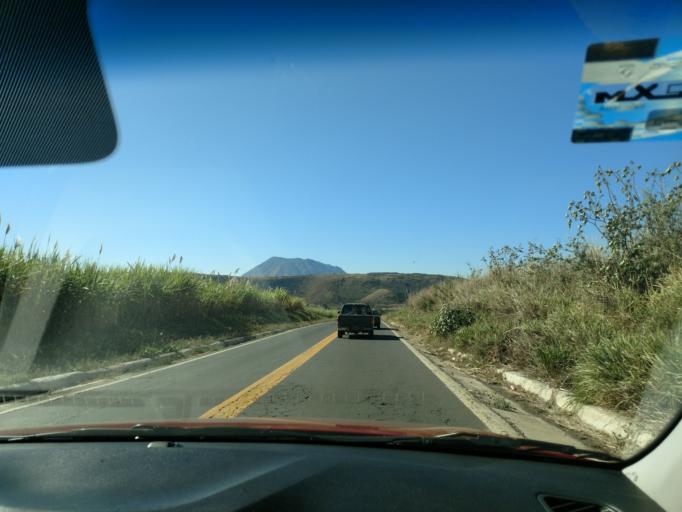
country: MX
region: Nayarit
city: San Pedro Lagunillas
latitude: 21.1507
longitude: -104.6128
